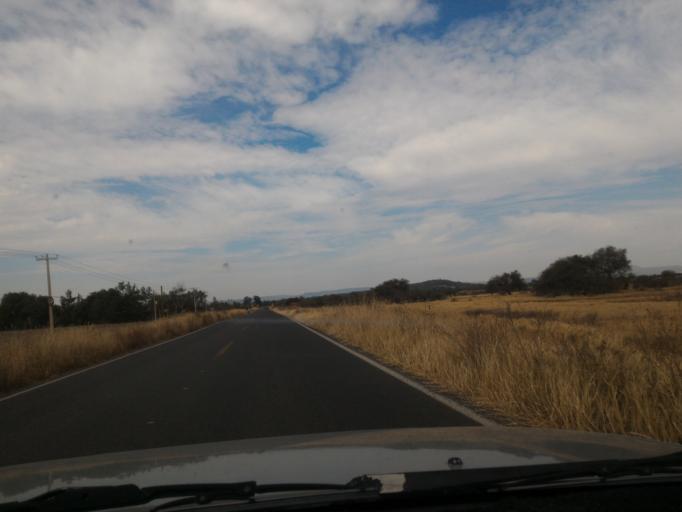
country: MX
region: Guanajuato
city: Ciudad Manuel Doblado
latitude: 20.7780
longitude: -101.9771
